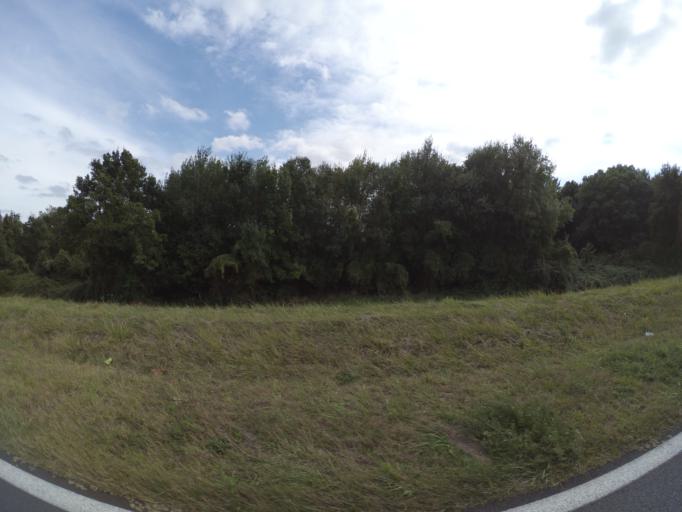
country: FR
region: Centre
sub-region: Departement d'Indre-et-Loire
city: Langeais
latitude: 47.2893
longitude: 0.3287
